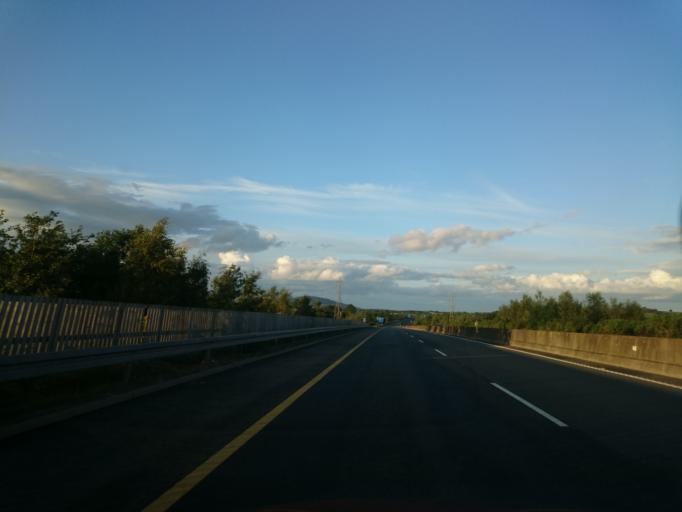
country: IE
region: Leinster
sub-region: Loch Garman
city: Gorey
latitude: 52.6529
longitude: -6.3099
